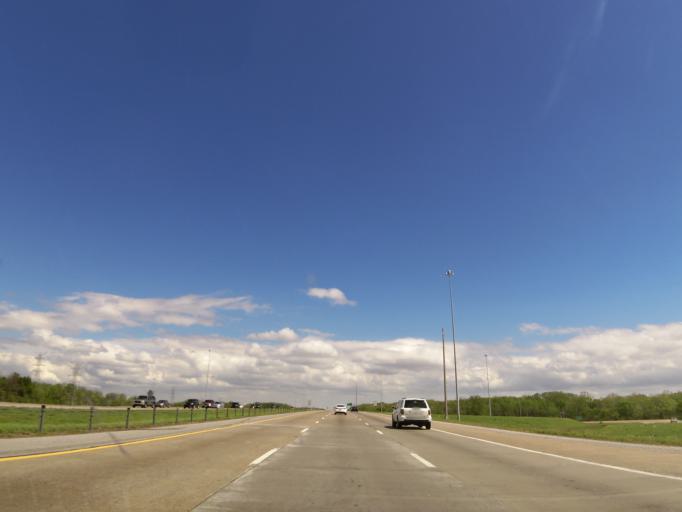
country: US
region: Tennessee
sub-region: Shelby County
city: Memphis
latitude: 35.1919
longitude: -89.9804
